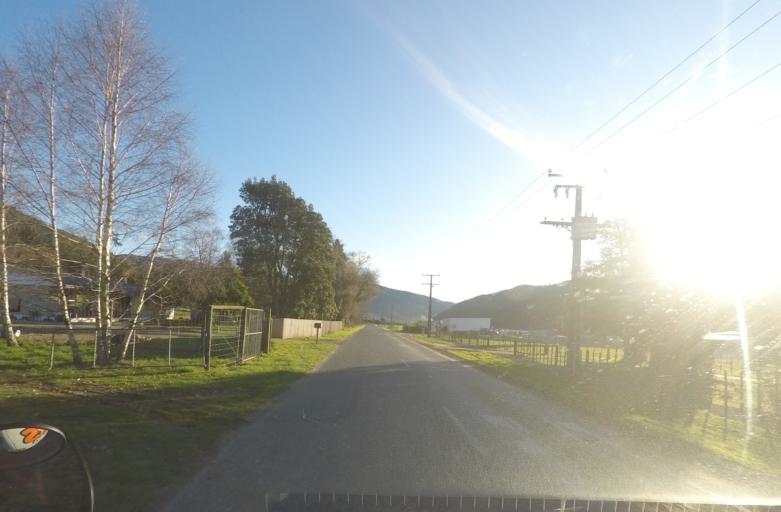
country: NZ
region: Marlborough
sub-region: Marlborough District
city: Picton
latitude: -41.2893
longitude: 173.8516
